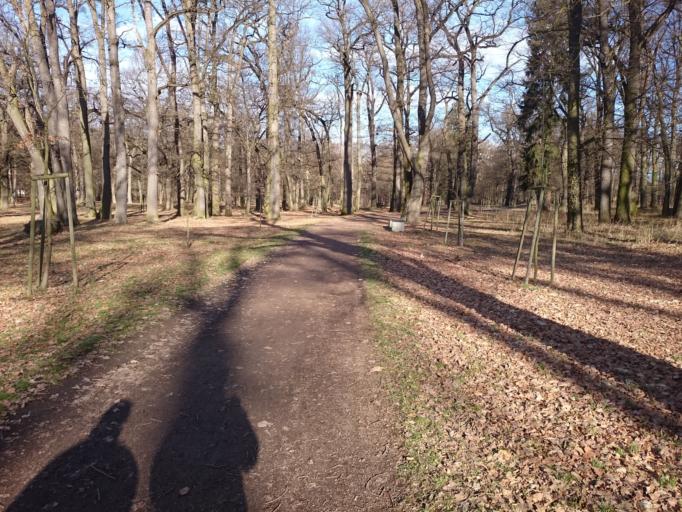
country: CZ
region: Pardubicky
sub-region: Okres Chrudim
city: Hermanuv Mestec
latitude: 49.9470
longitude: 15.6773
